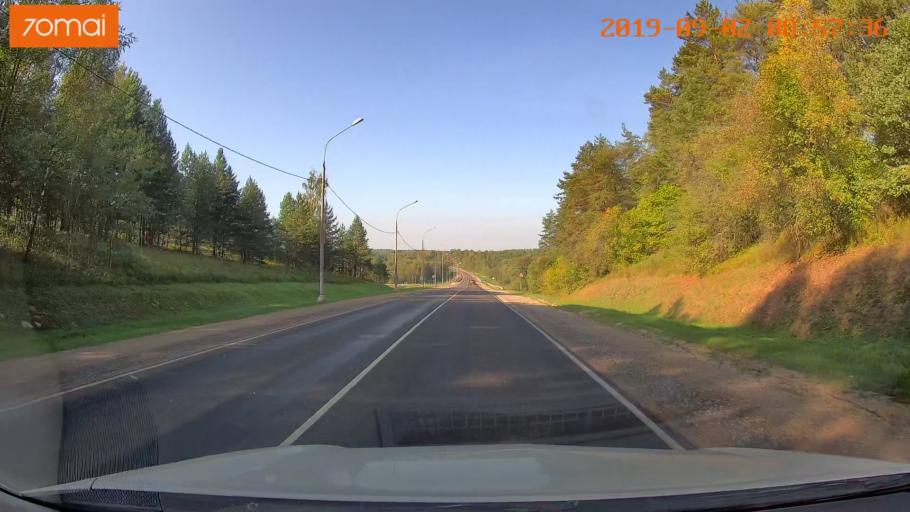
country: RU
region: Kaluga
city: Myatlevo
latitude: 54.9355
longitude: 35.7644
